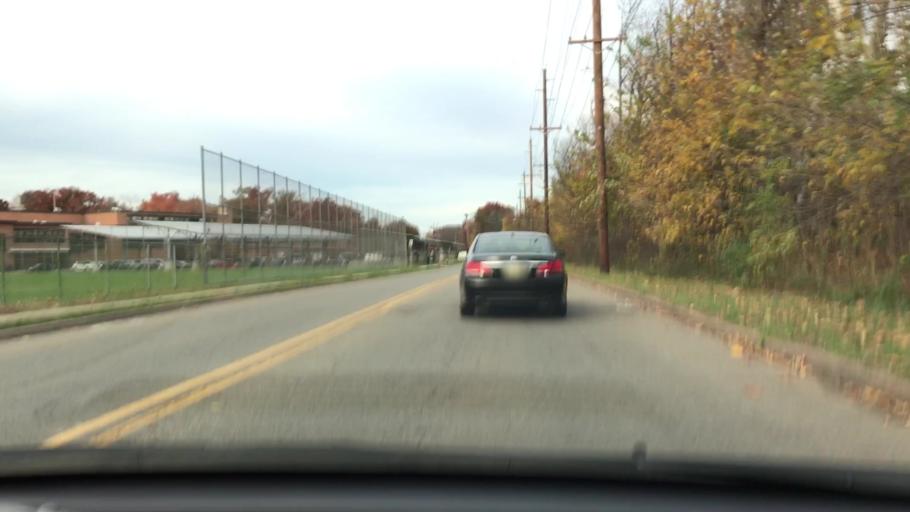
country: US
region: New Jersey
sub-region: Bergen County
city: Teaneck
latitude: 40.8979
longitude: -74.0114
